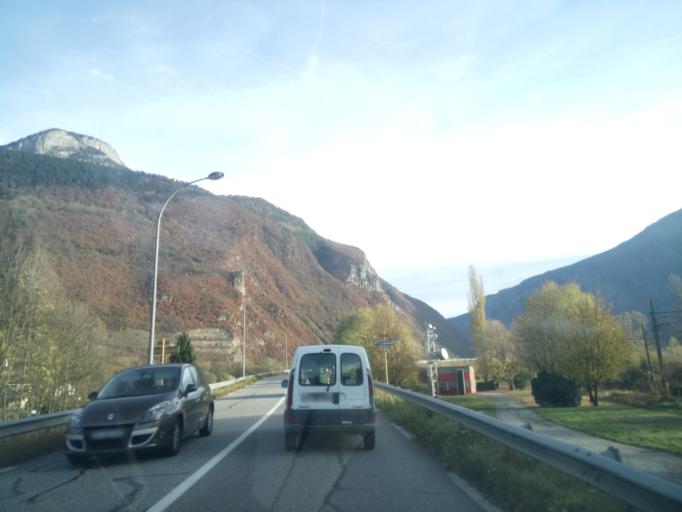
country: FR
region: Rhone-Alpes
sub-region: Departement de la Savoie
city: La Chambre
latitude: 45.3510
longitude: 6.3057
